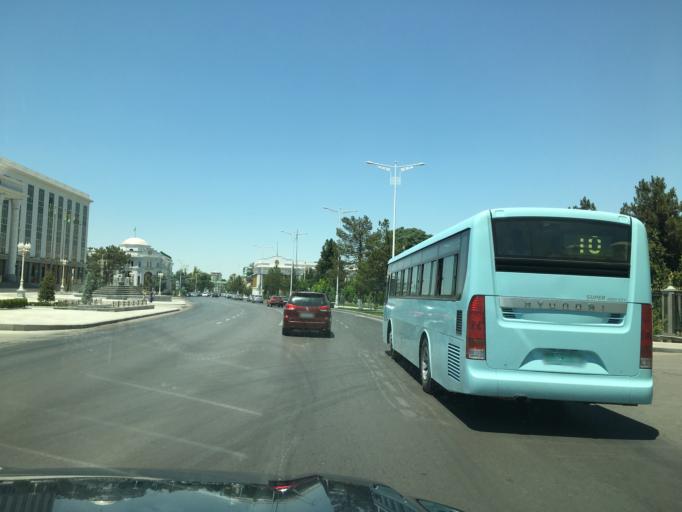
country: TM
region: Ahal
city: Ashgabat
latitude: 37.9388
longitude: 58.3830
